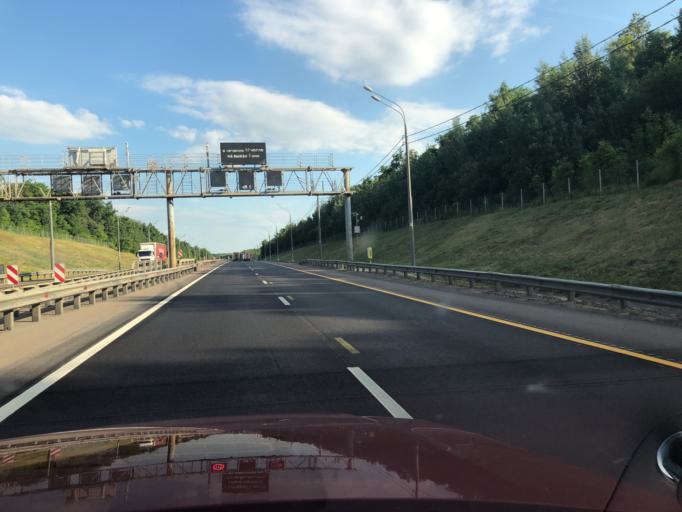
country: RU
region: Lipetsk
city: Zadonsk
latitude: 52.4003
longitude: 38.8592
